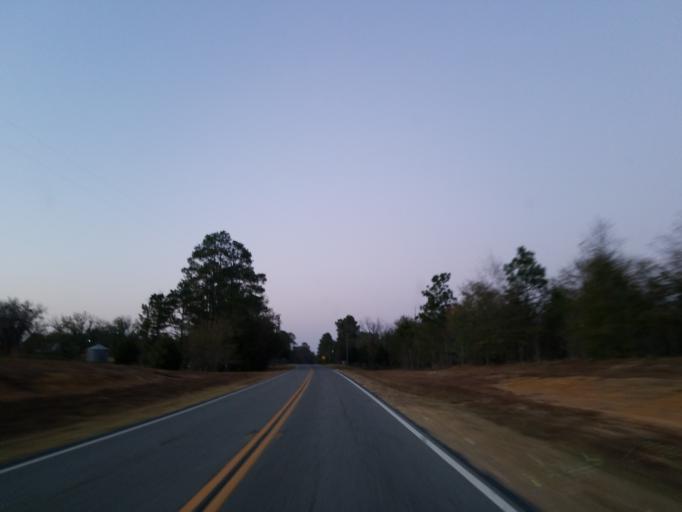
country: US
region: Georgia
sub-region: Wilcox County
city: Rochelle
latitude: 31.8437
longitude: -83.5628
